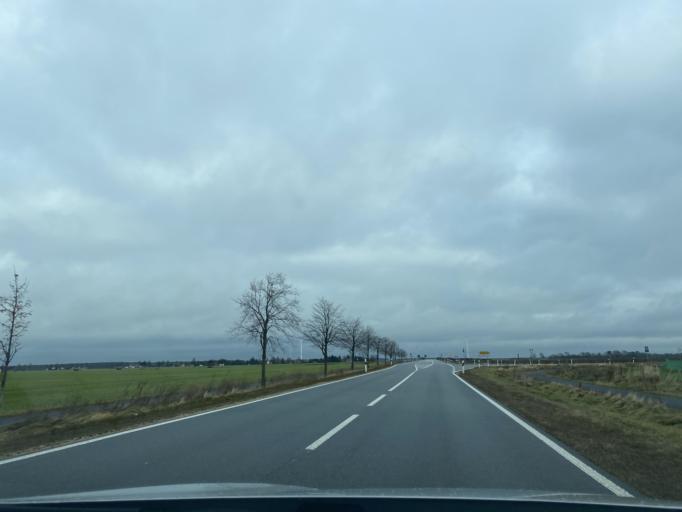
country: PL
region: Lower Silesian Voivodeship
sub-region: Powiat zgorzelecki
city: Piensk
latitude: 51.2327
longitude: 14.9779
